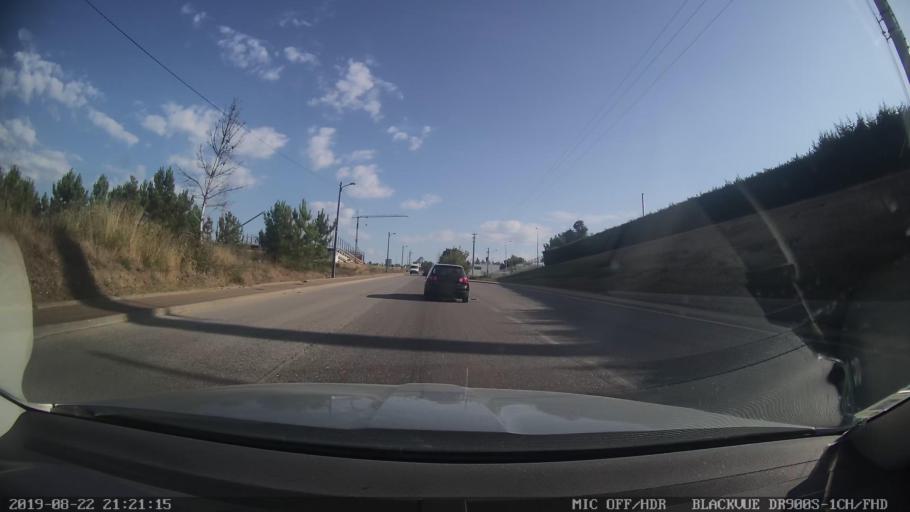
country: PT
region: Castelo Branco
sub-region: Serta
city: Serta
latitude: 39.8174
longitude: -8.1087
